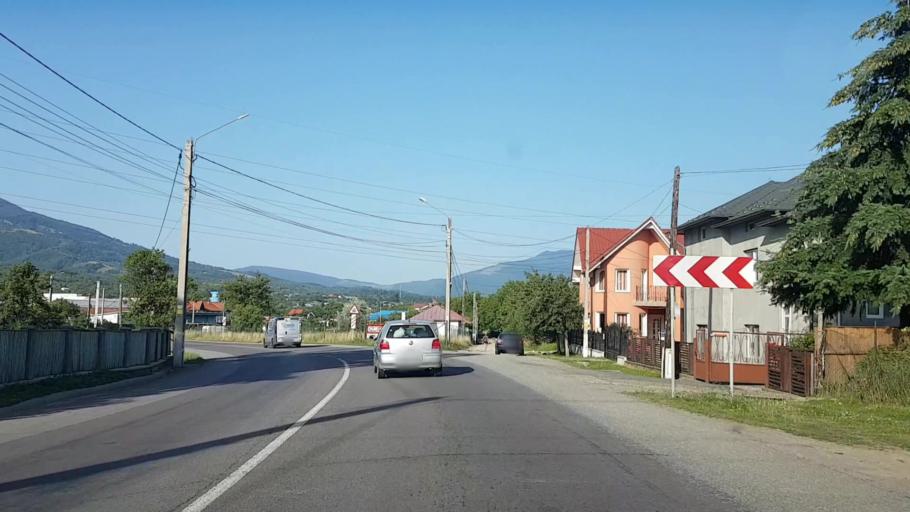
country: RO
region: Bistrita-Nasaud
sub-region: Comuna Prundu Bargaului
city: Susenii Bargaului
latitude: 47.2173
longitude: 24.7084
